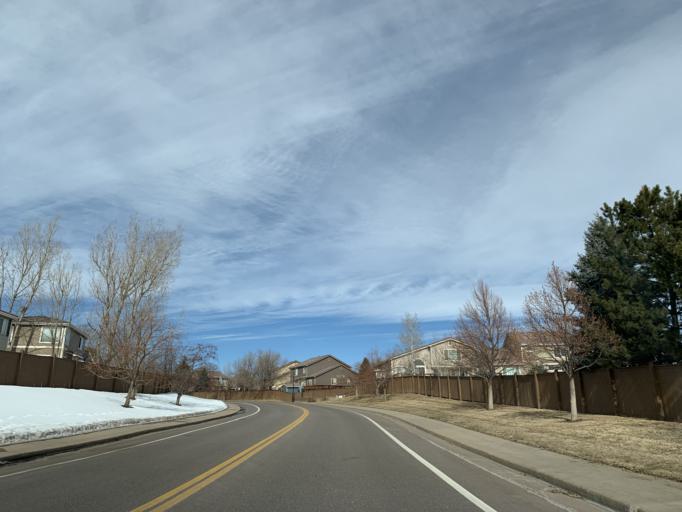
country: US
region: Colorado
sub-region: Douglas County
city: Carriage Club
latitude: 39.5314
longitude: -104.9351
